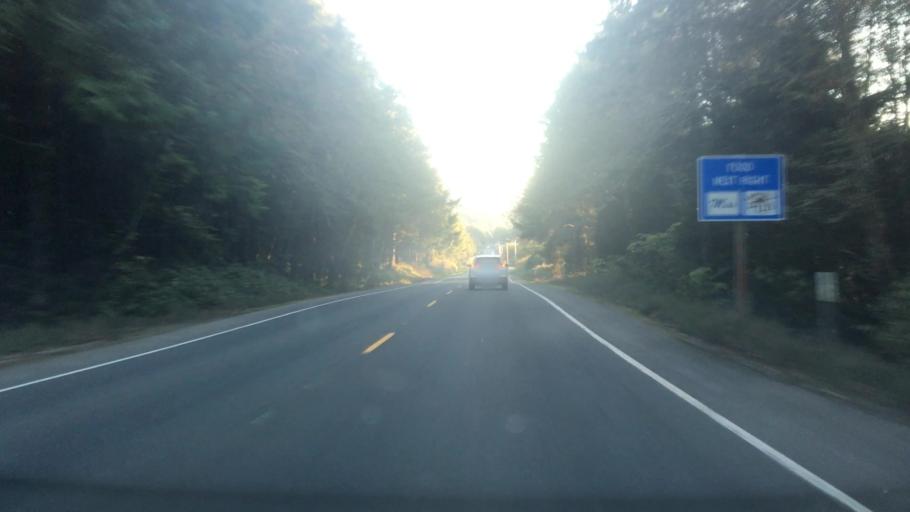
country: US
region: Oregon
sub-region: Clatsop County
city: Cannon Beach
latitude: 45.8767
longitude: -123.9578
